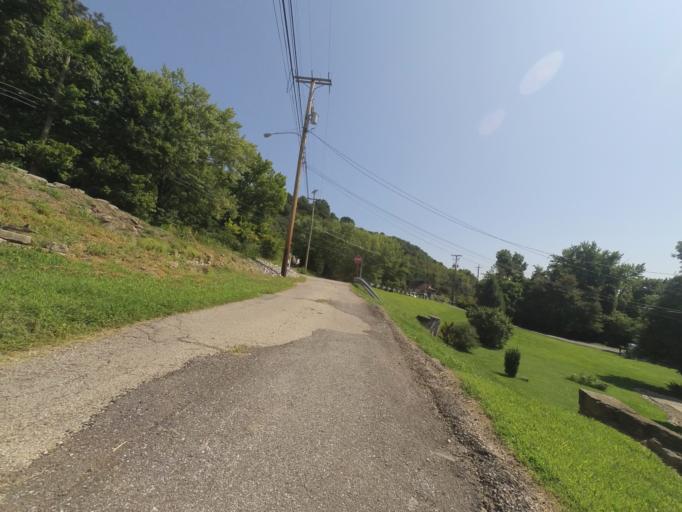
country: US
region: West Virginia
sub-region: Cabell County
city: Huntington
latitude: 38.4299
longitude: -82.4413
